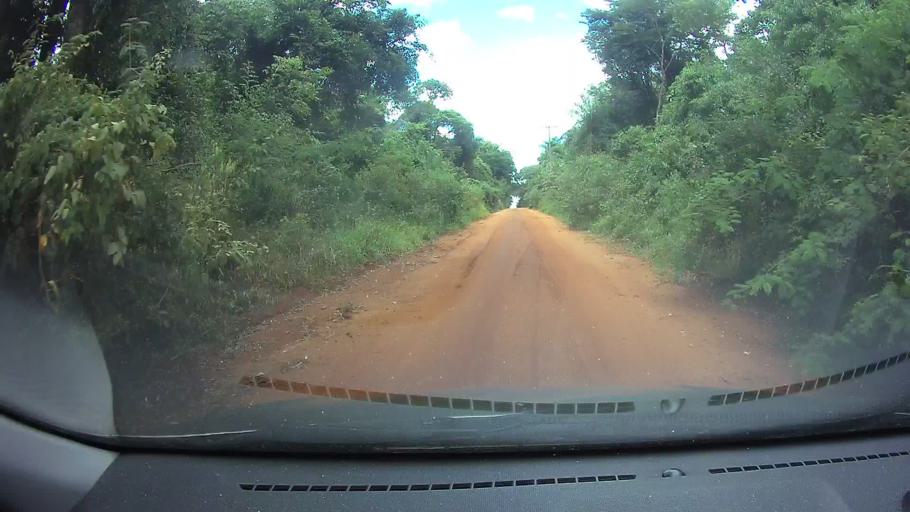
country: PY
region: Paraguari
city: La Colmena
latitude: -25.9445
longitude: -56.7800
